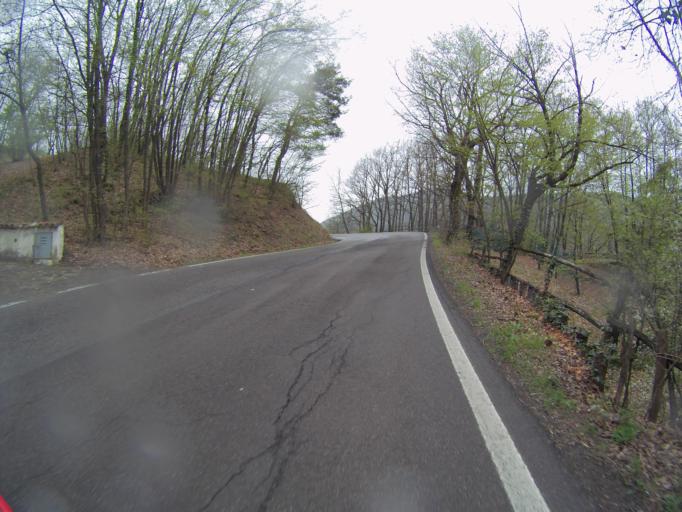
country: IT
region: Emilia-Romagna
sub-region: Provincia di Reggio Emilia
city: Ciano d'Enza
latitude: 44.5700
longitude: 10.4067
